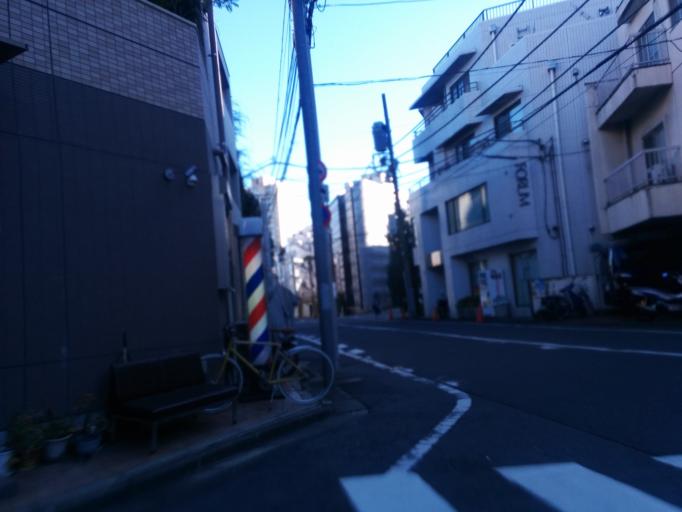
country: JP
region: Tokyo
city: Tokyo
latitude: 35.6769
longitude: 139.7068
